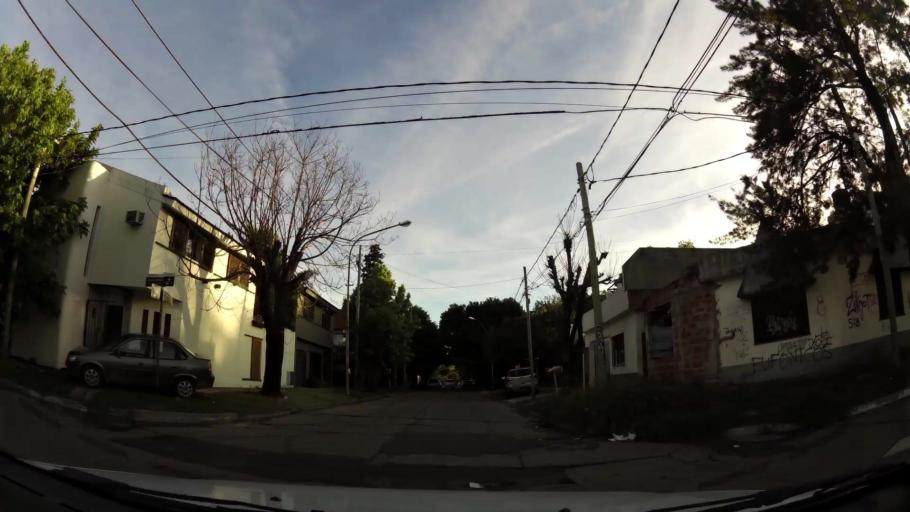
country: AR
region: Buenos Aires
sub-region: Partido de Moron
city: Moron
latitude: -34.6421
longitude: -58.6379
